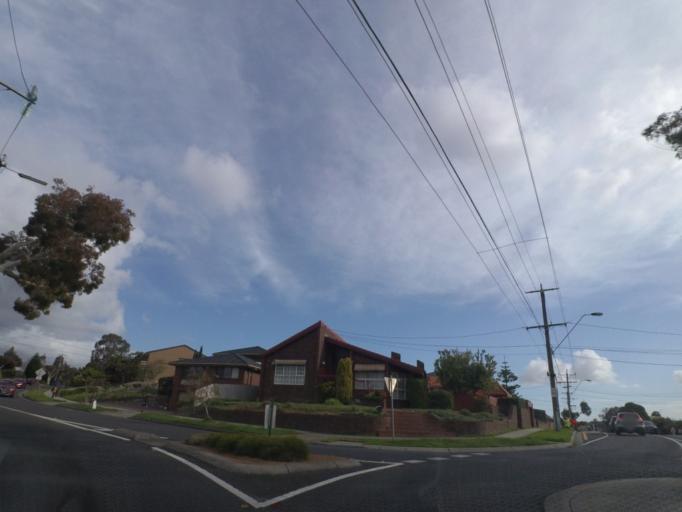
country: AU
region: Victoria
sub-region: Whitehorse
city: Vermont South
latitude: -37.8486
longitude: 145.1810
